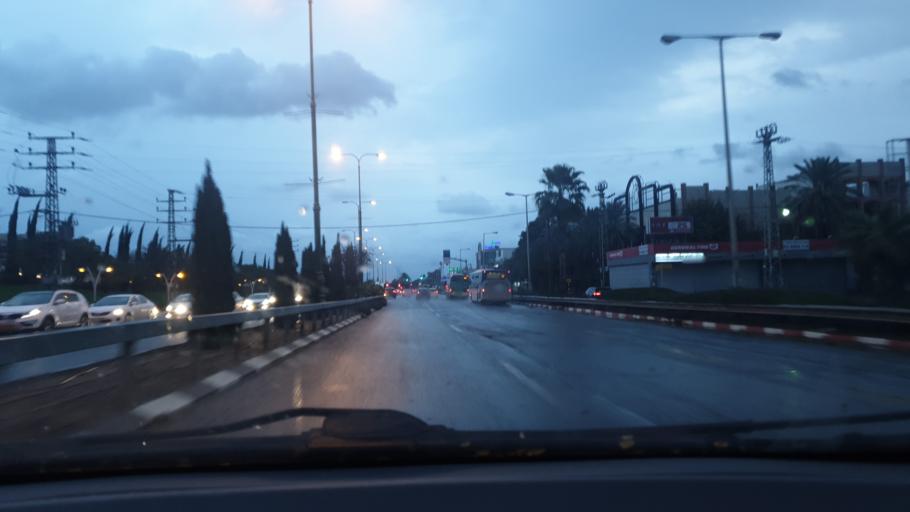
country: IL
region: Central District
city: Rishon LeZiyyon
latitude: 31.9781
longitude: 34.8084
